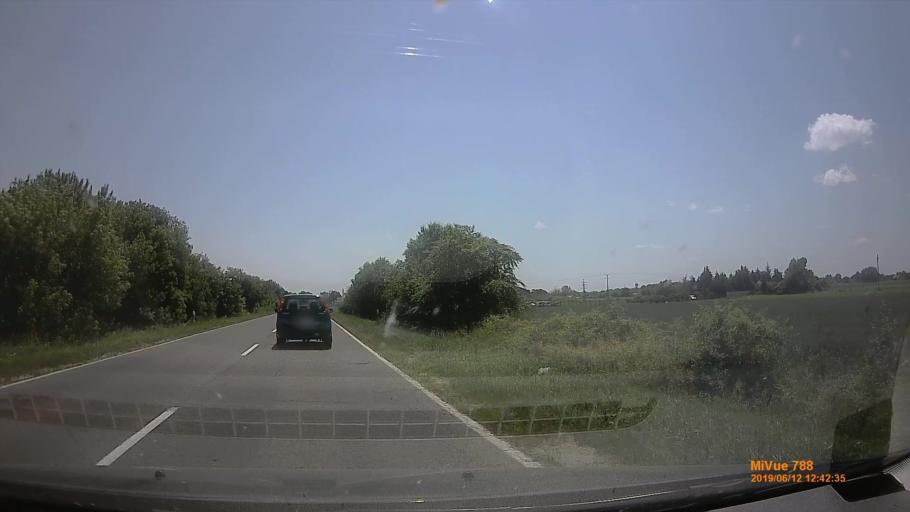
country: HU
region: Bacs-Kiskun
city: Kiskunfelegyhaza
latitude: 46.7364
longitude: 19.8408
